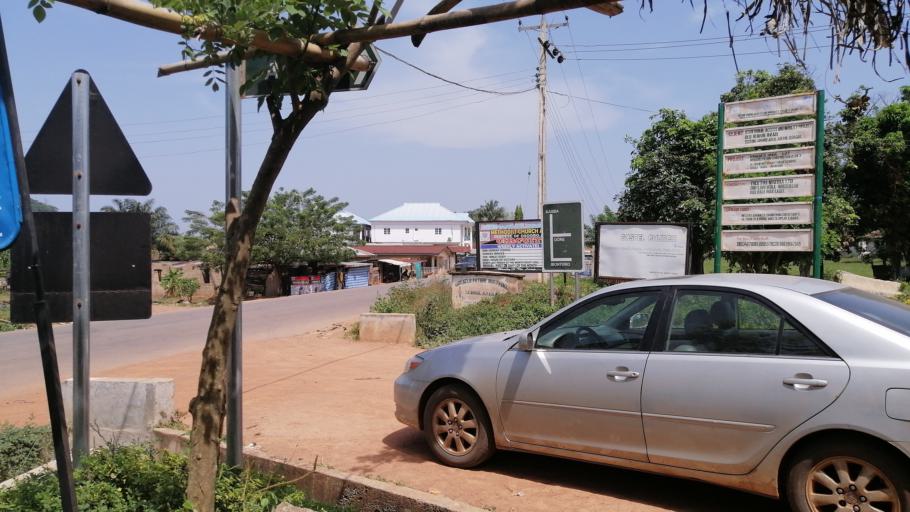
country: NG
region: Osun
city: Iragbiji
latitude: 7.8932
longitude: 4.7021
